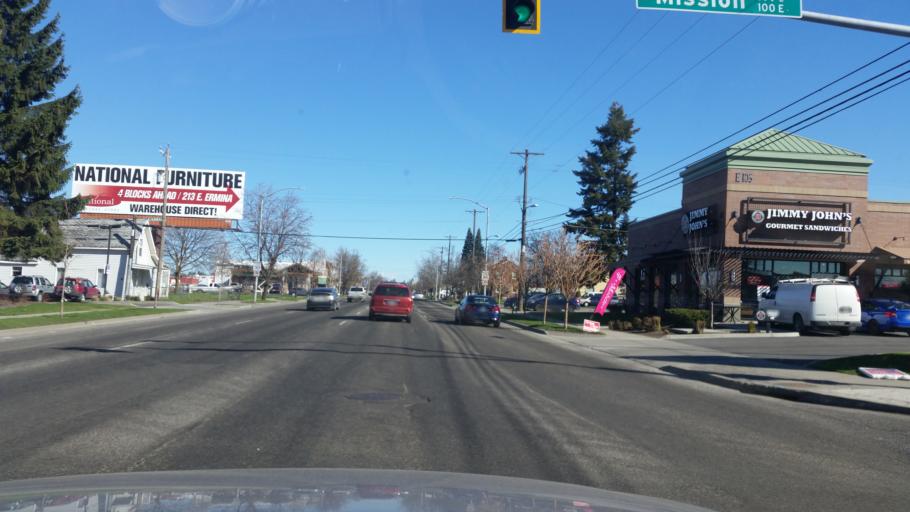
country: US
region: Washington
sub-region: Spokane County
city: Spokane
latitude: 47.6714
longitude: -117.4095
